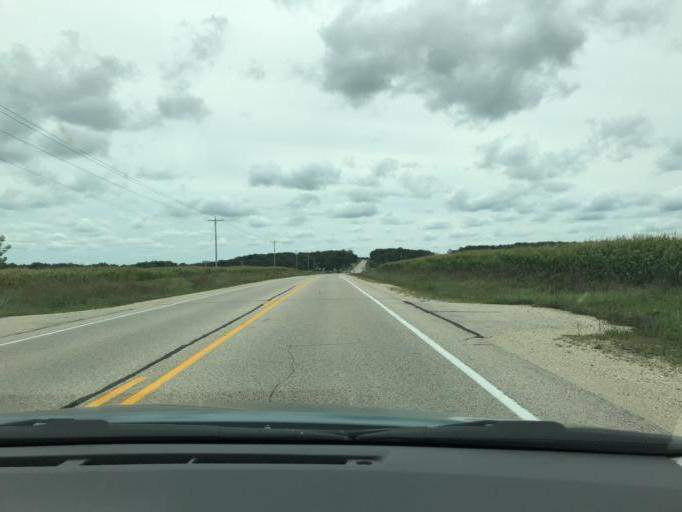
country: US
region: Wisconsin
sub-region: Racine County
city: Bohners Lake
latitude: 42.6144
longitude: -88.2326
